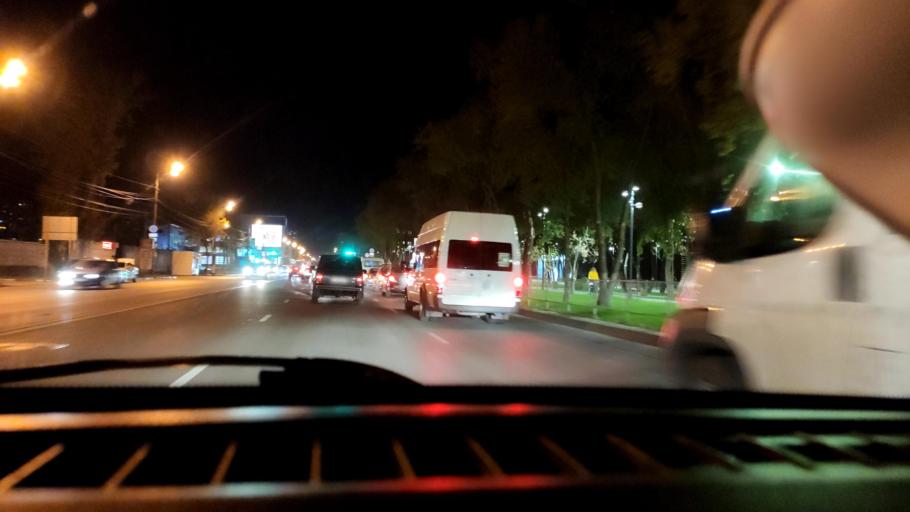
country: RU
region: Samara
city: Samara
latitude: 53.1953
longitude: 50.1906
